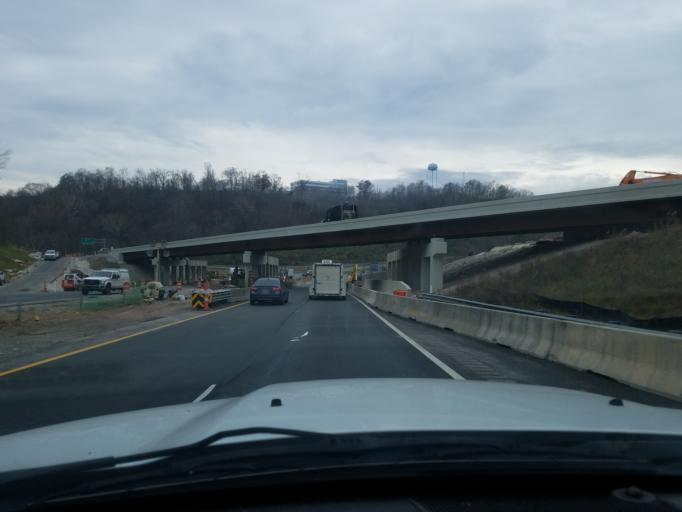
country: US
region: West Virginia
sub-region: Cabell County
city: Huntington
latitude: 38.3944
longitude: -82.4514
